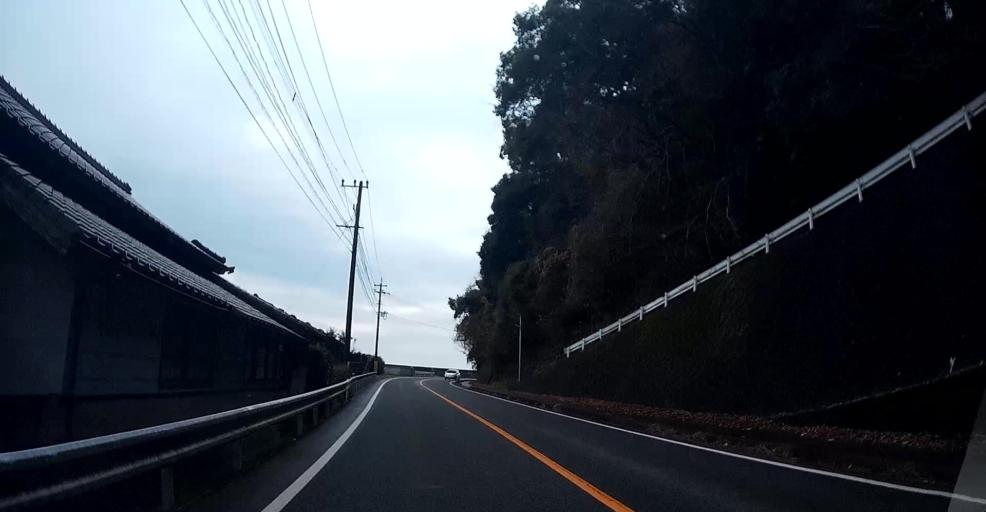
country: JP
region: Kumamoto
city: Matsubase
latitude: 32.6396
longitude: 130.6422
